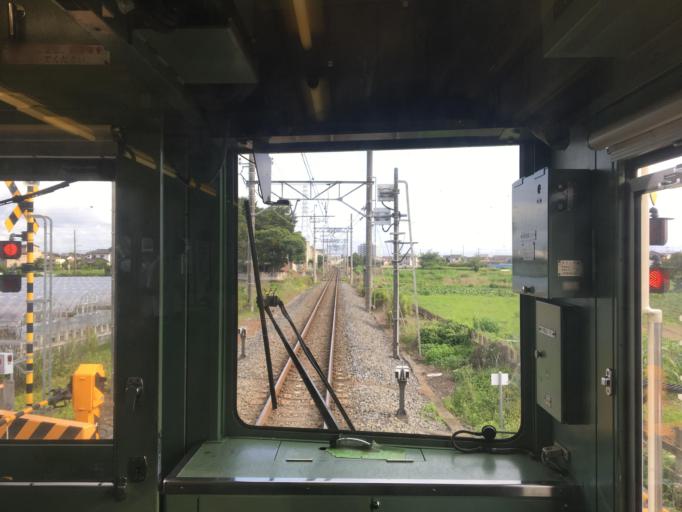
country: JP
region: Tochigi
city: Ashikaga
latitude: 36.3150
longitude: 139.4552
